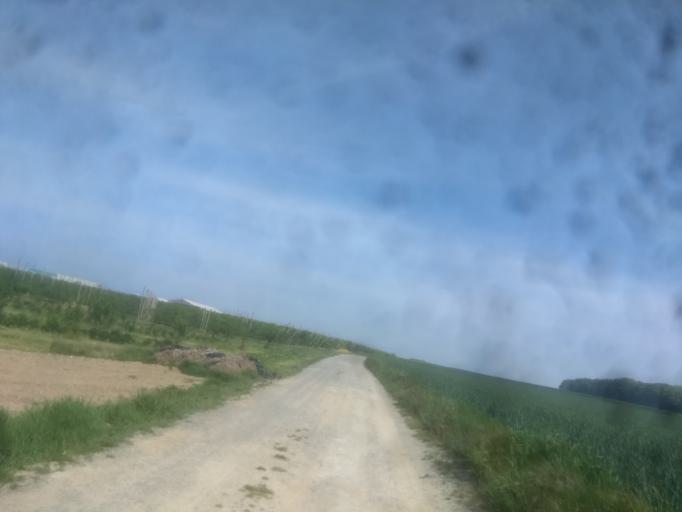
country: FR
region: Nord-Pas-de-Calais
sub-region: Departement du Pas-de-Calais
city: Beaurains
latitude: 50.2609
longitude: 2.8074
